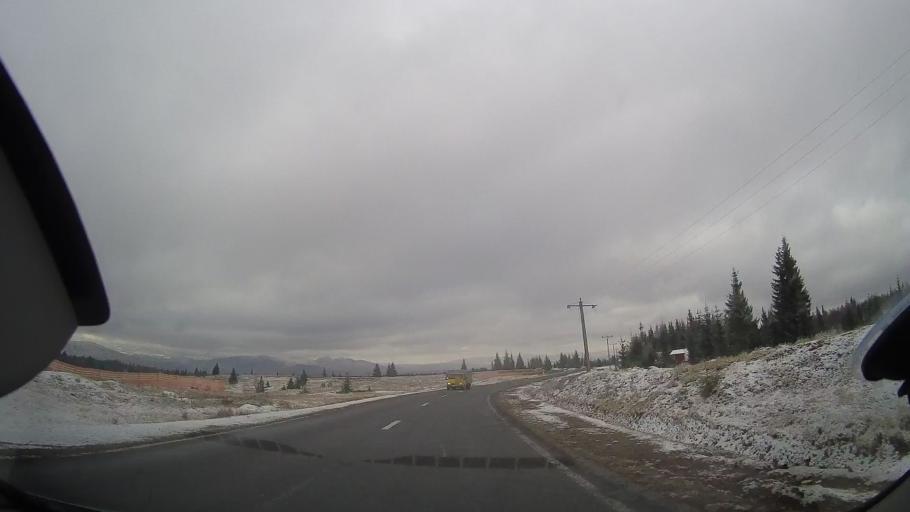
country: RO
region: Cluj
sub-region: Comuna Belis
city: Belis
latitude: 46.6979
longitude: 23.0368
